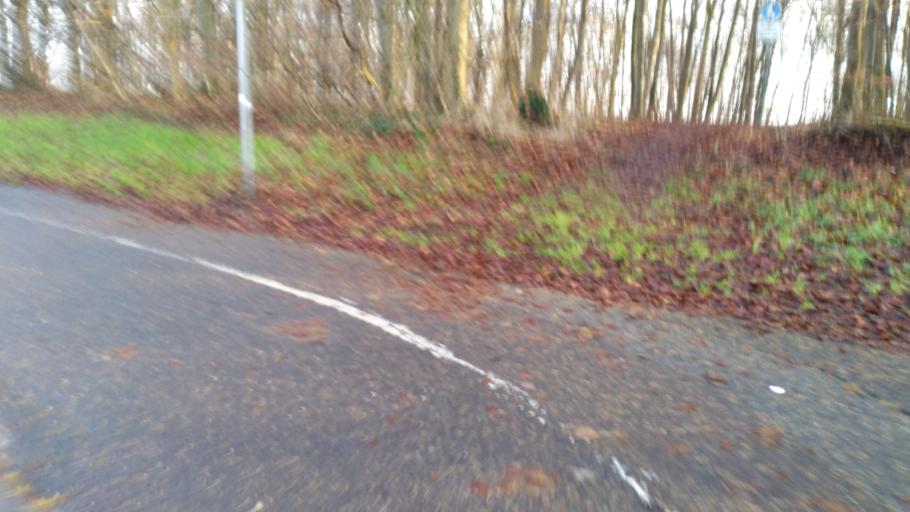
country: DE
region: Mecklenburg-Vorpommern
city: Selmsdorf
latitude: 53.9119
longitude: 10.7984
